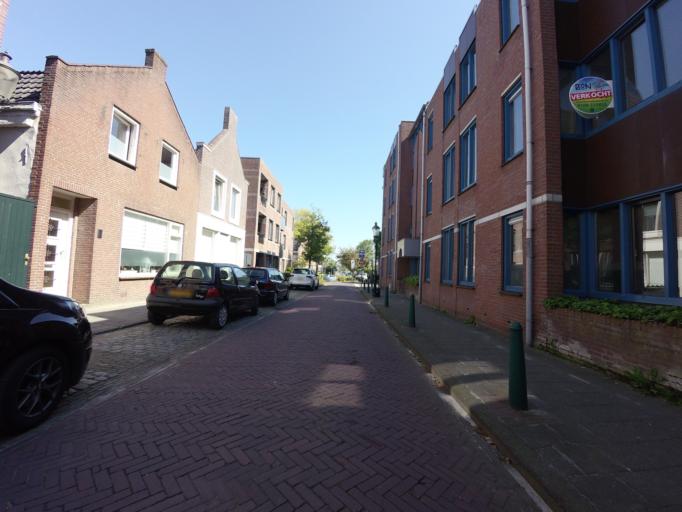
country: NL
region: North Brabant
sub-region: Gemeente Moerdijk
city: Klundert
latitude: 51.6435
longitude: 4.6093
